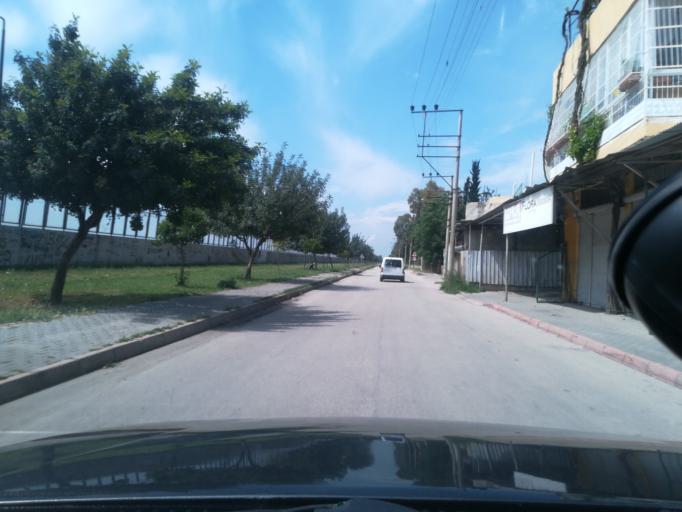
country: TR
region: Adana
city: Seyhan
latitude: 36.9842
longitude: 35.2807
